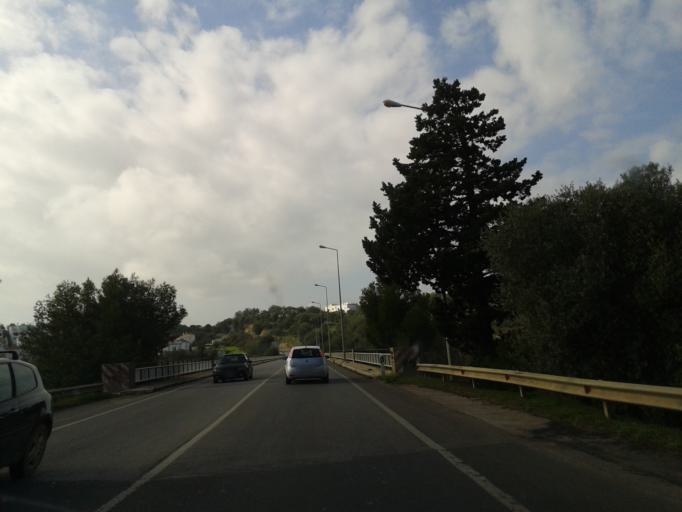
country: PT
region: Faro
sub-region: Tavira
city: Tavira
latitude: 37.1323
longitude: -7.6538
